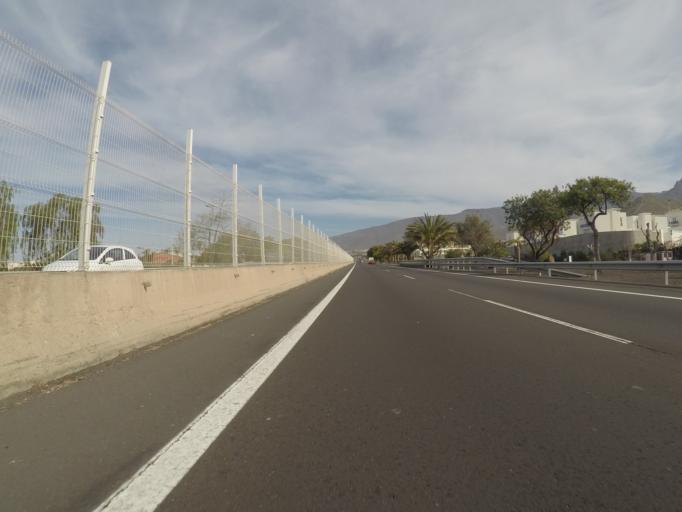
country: ES
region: Canary Islands
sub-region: Provincia de Santa Cruz de Tenerife
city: Playa de las Americas
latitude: 28.0881
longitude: -16.7289
